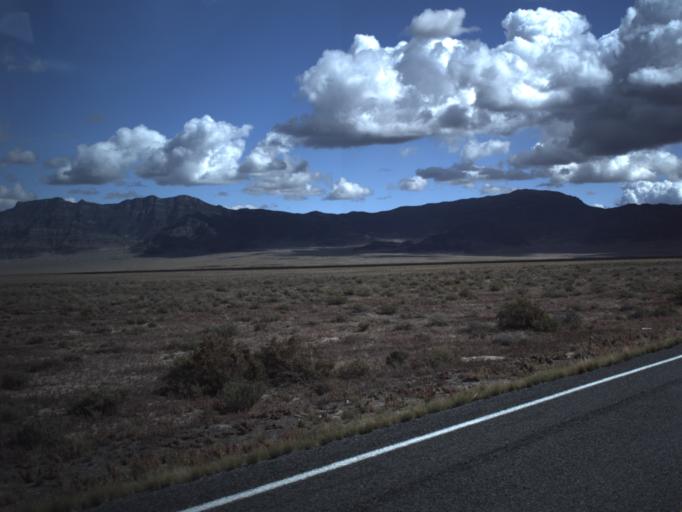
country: US
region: Utah
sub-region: Beaver County
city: Milford
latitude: 38.5467
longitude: -113.7207
